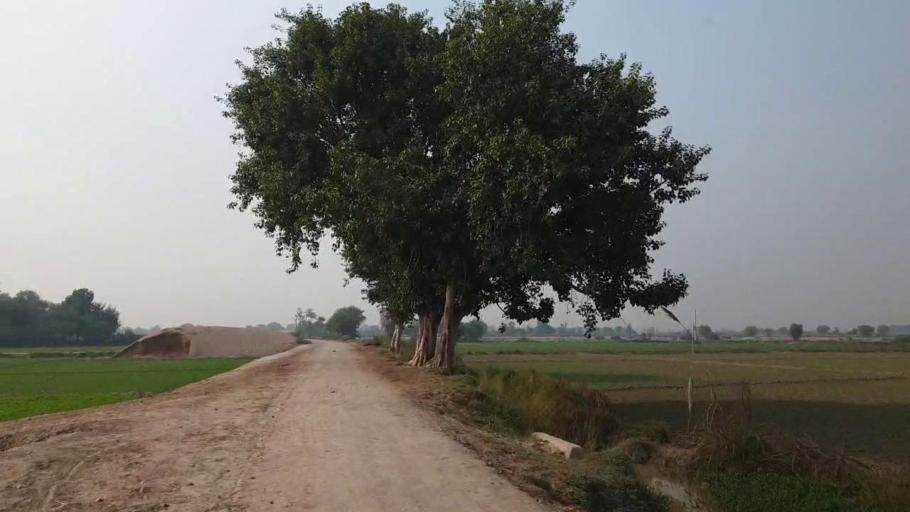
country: PK
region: Sindh
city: Bhan
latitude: 26.5420
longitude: 67.7121
